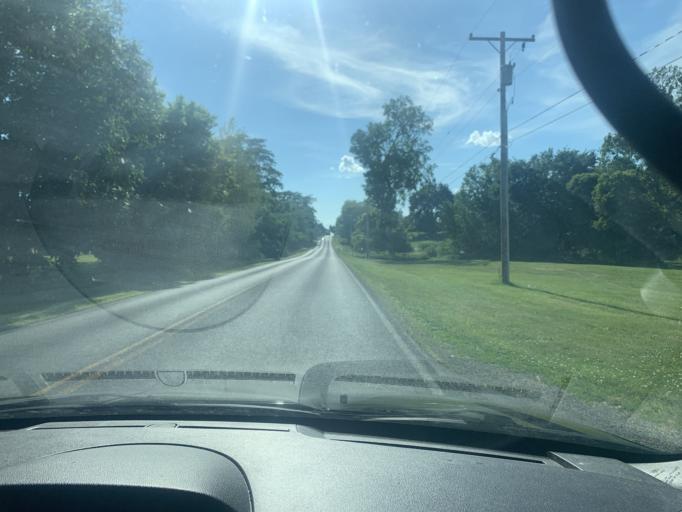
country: US
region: Ohio
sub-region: Logan County
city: Bellefontaine
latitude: 40.3483
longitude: -83.7876
